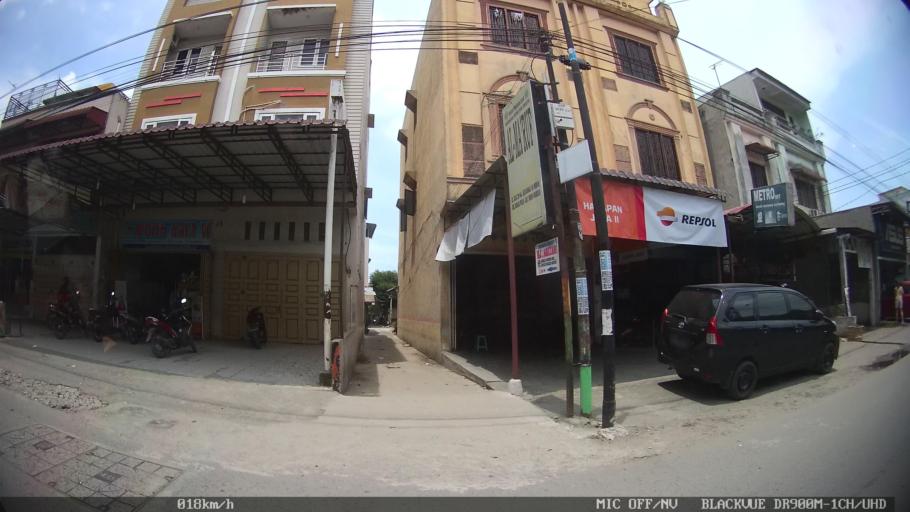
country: ID
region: North Sumatra
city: Labuhan Deli
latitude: 3.6894
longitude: 98.6585
